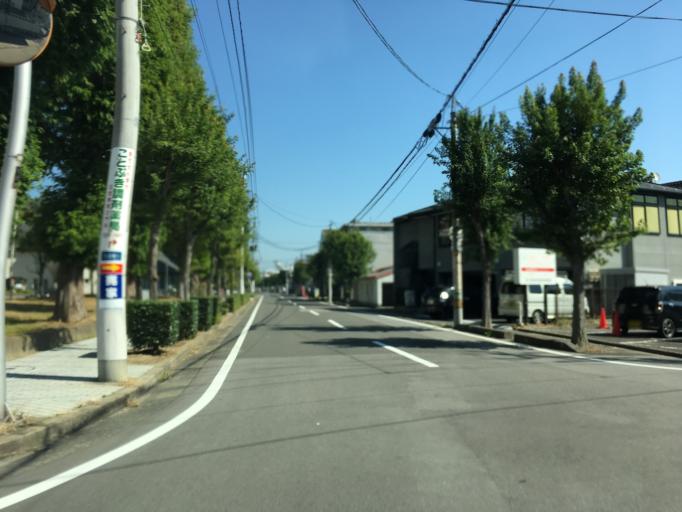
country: JP
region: Fukushima
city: Fukushima-shi
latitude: 37.7688
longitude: 140.4787
